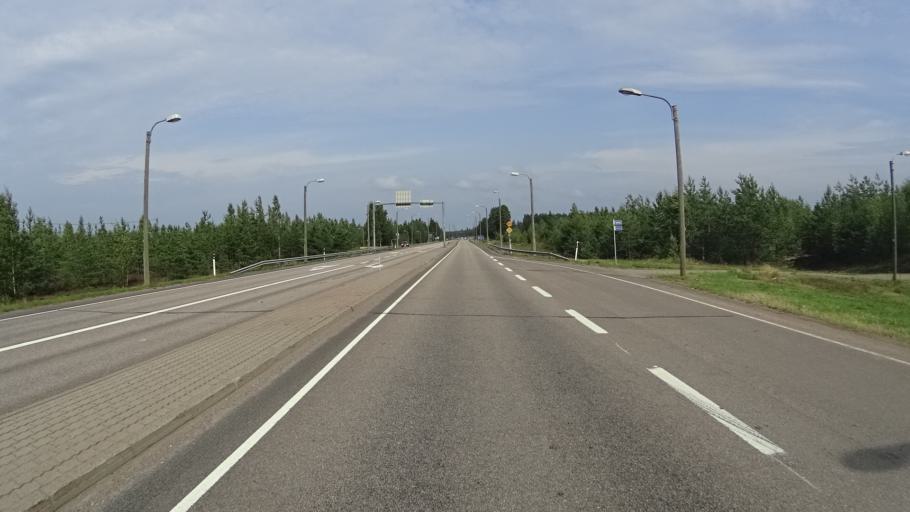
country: FI
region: Kymenlaakso
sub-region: Kouvola
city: Kouvola
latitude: 60.8949
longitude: 26.9108
